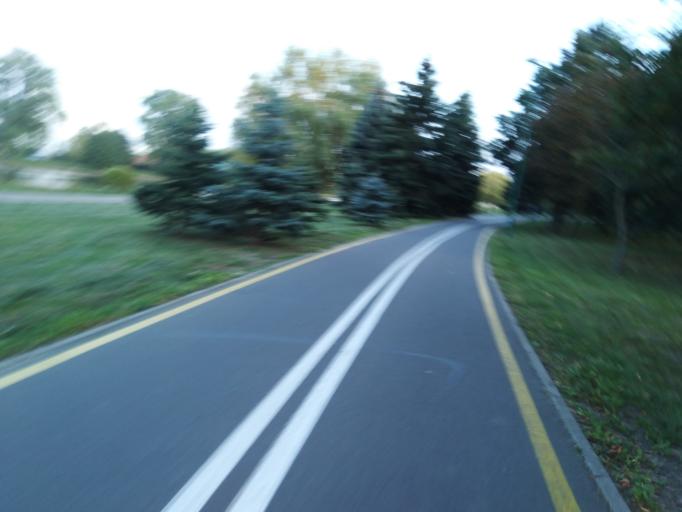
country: BY
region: Minsk
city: Minsk
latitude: 53.9327
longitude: 27.5283
